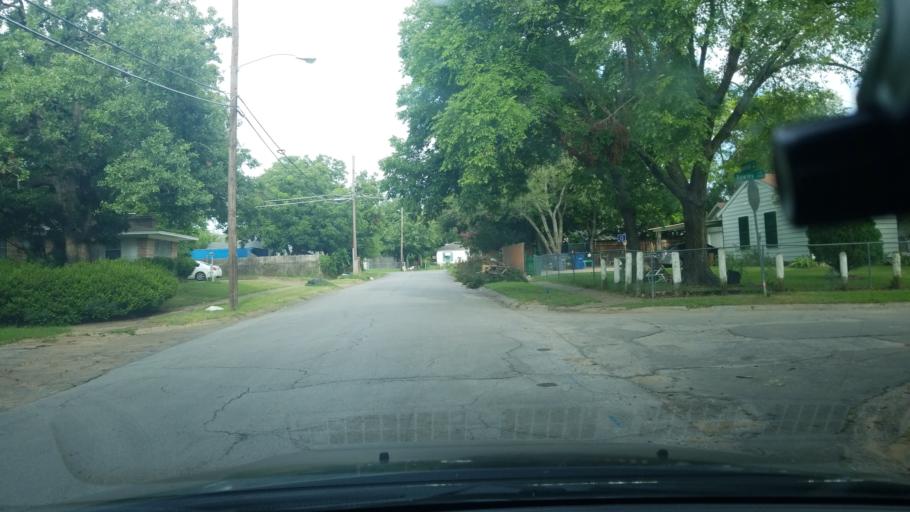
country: US
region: Texas
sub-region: Dallas County
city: Balch Springs
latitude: 32.7378
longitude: -96.6731
